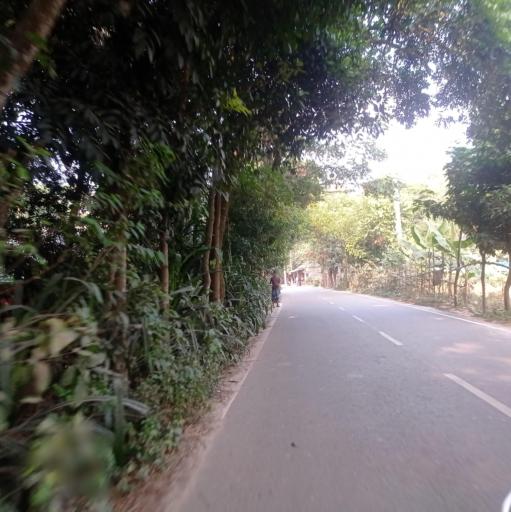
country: BD
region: Dhaka
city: Bhairab Bazar
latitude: 24.0953
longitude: 90.8526
